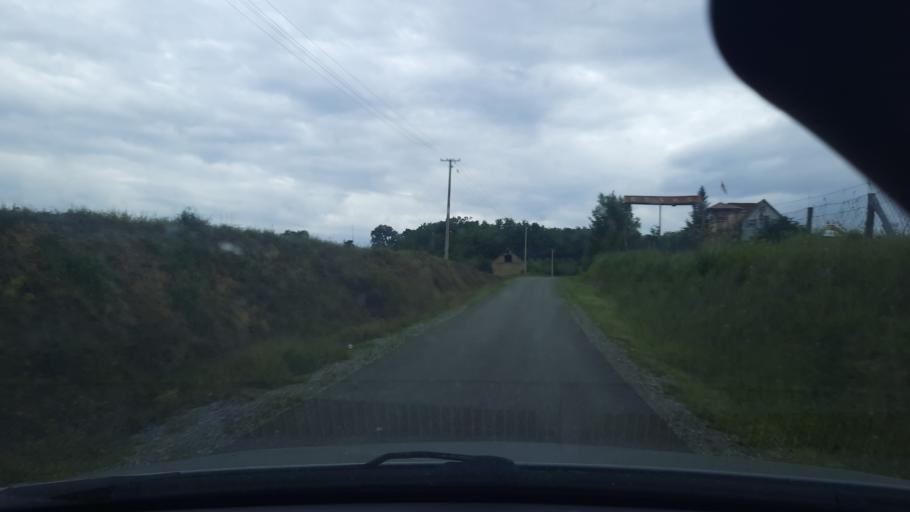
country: RS
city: Jarebice
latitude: 44.4916
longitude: 19.4791
